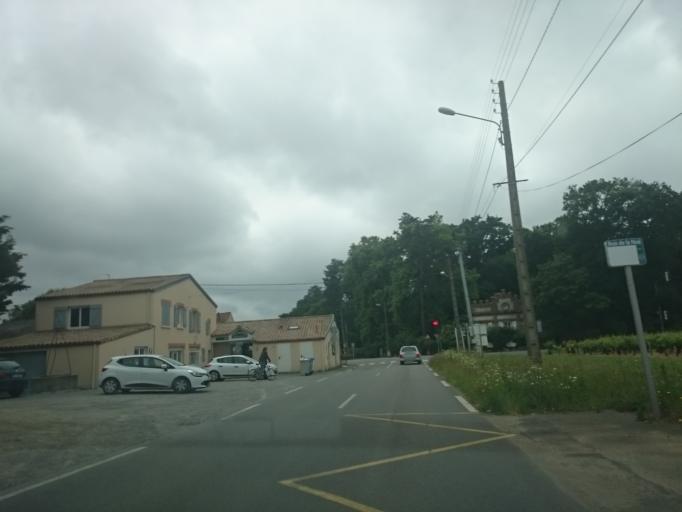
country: FR
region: Pays de la Loire
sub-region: Departement de la Loire-Atlantique
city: Bouaye
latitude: 47.1426
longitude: -1.6720
